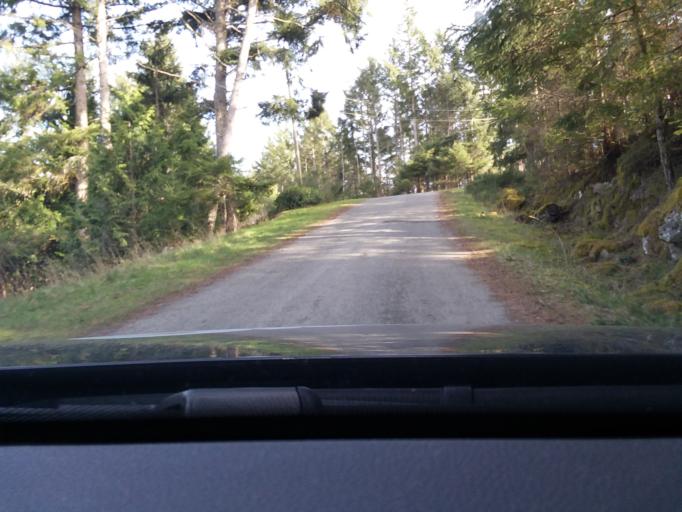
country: CA
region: British Columbia
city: North Saanich
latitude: 48.7701
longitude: -123.2964
